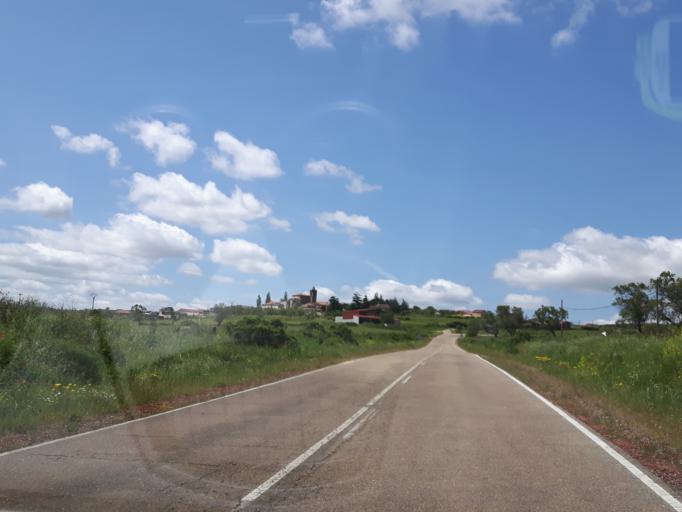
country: ES
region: Castille and Leon
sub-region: Provincia de Salamanca
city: Aldea del Obispo
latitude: 40.7119
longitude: -6.7880
